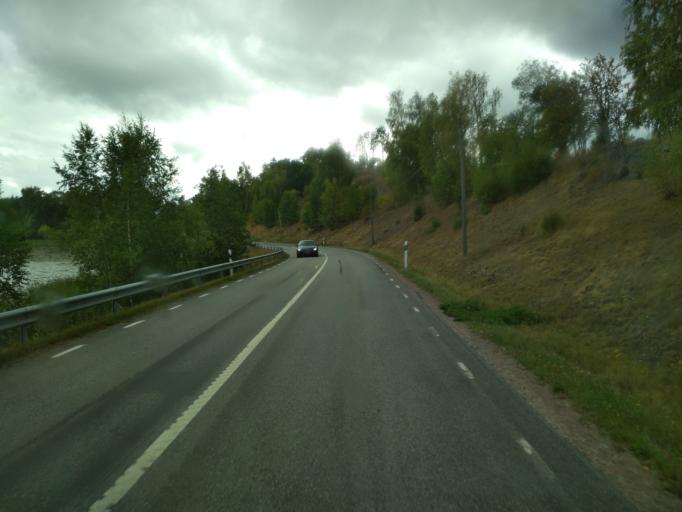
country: SE
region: Vaestmanland
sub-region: Surahammars Kommun
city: Surahammar
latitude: 59.6998
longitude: 16.1890
